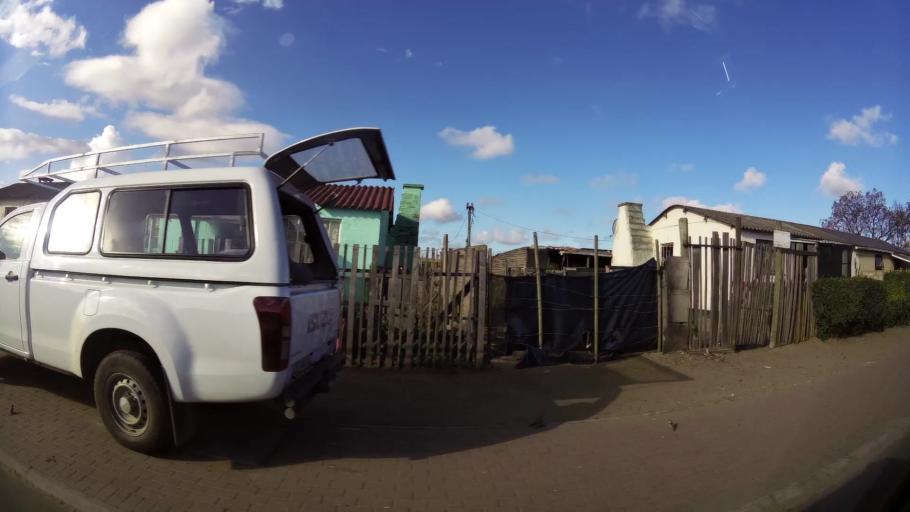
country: ZA
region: Western Cape
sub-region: Eden District Municipality
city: George
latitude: -33.9848
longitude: 22.4761
